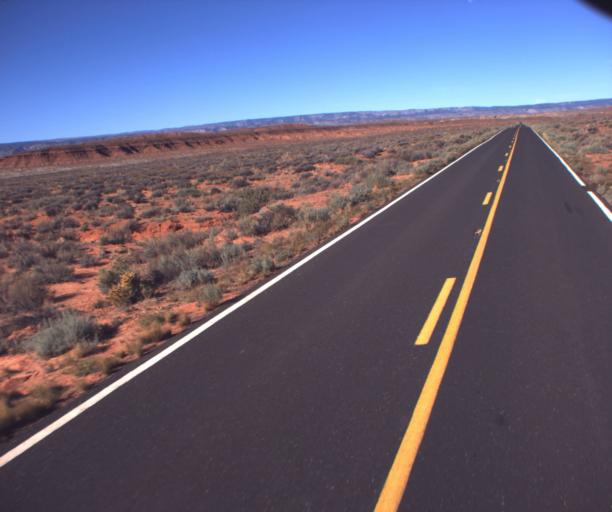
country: US
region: Arizona
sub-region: Coconino County
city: Page
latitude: 36.6849
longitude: -111.8587
